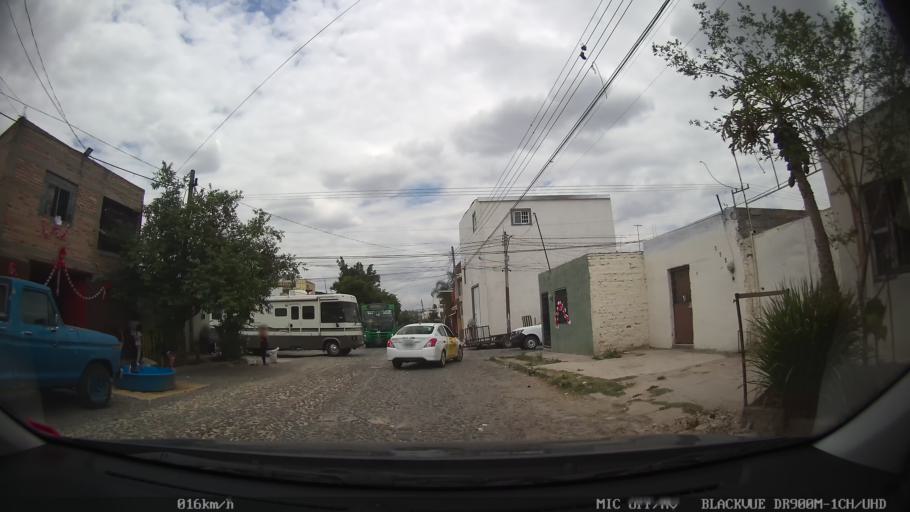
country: MX
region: Jalisco
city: Tlaquepaque
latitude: 20.6523
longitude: -103.2623
